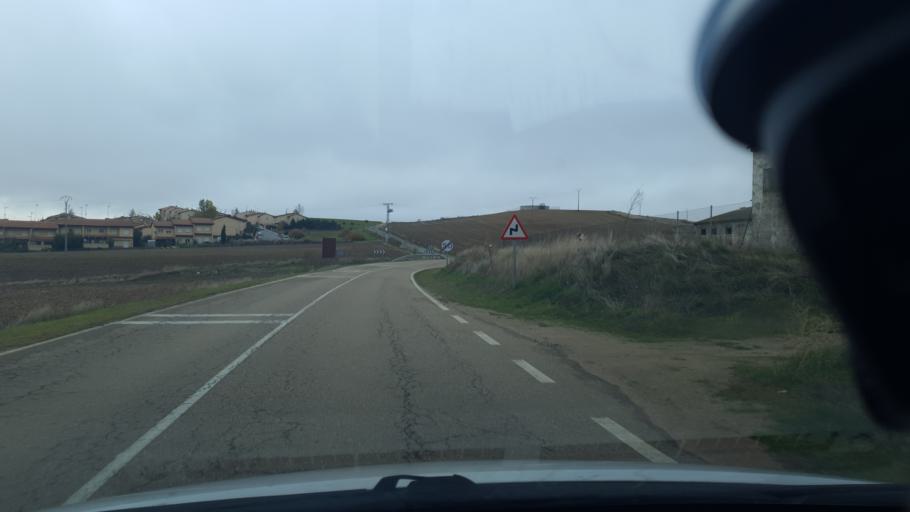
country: ES
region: Castille and Leon
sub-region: Provincia de Segovia
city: Hontanares de Eresma
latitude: 40.9855
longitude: -4.2026
